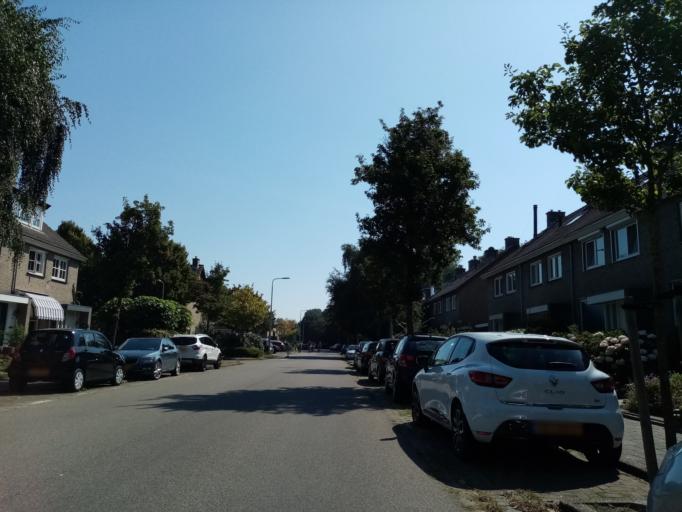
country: NL
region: South Holland
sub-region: Gemeente Lisse
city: Lisse
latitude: 52.2478
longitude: 4.5621
